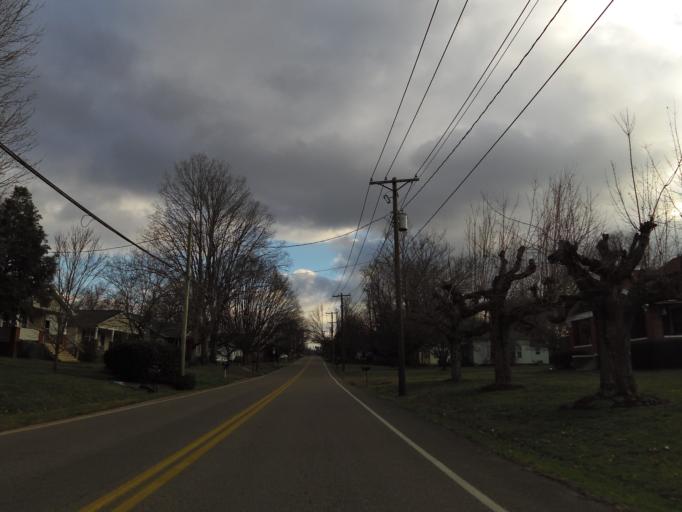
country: US
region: Tennessee
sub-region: Knox County
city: Knoxville
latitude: 35.9500
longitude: -83.8917
